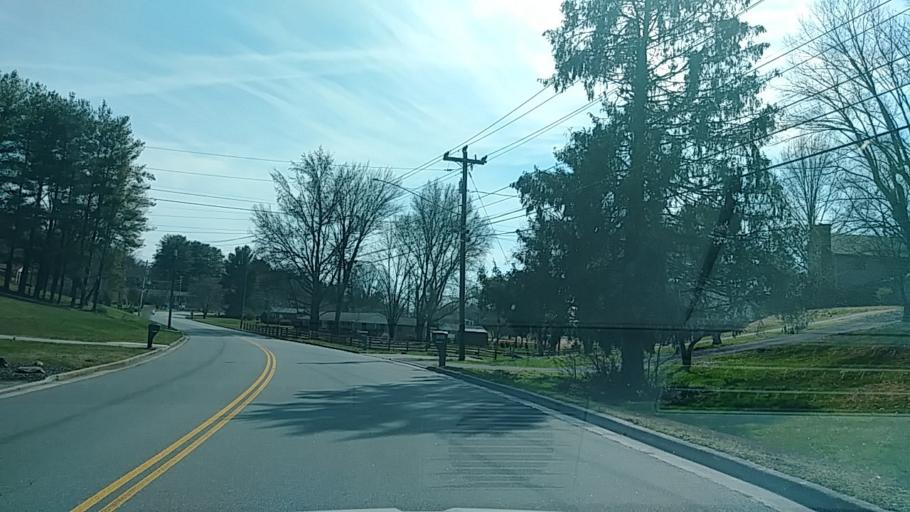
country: US
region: Tennessee
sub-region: Hamblen County
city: Morristown
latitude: 36.2183
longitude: -83.3216
